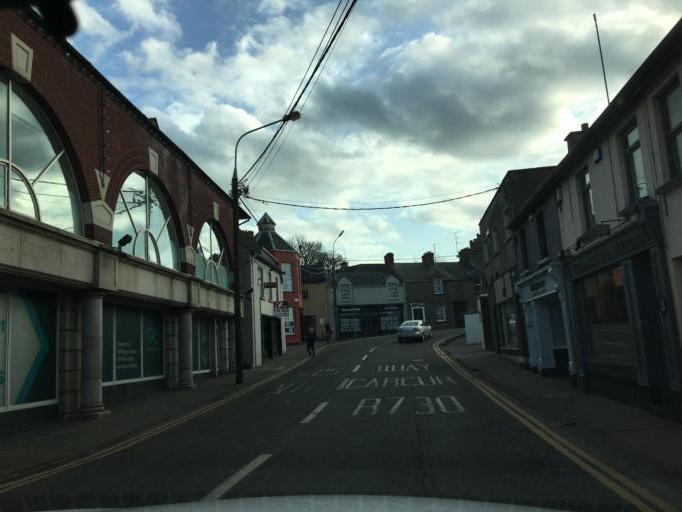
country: IE
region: Leinster
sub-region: Loch Garman
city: Loch Garman
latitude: 52.3423
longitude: -6.4651
